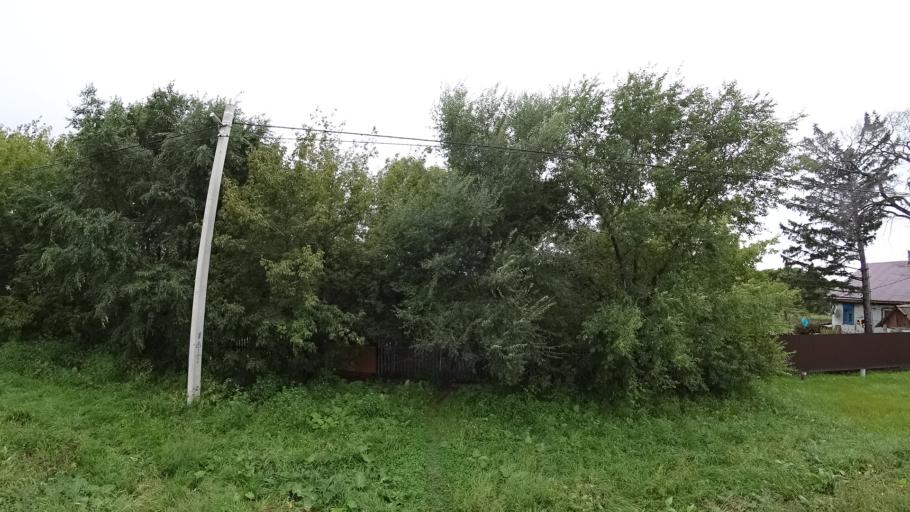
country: RU
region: Primorskiy
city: Monastyrishche
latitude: 44.0798
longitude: 132.5821
